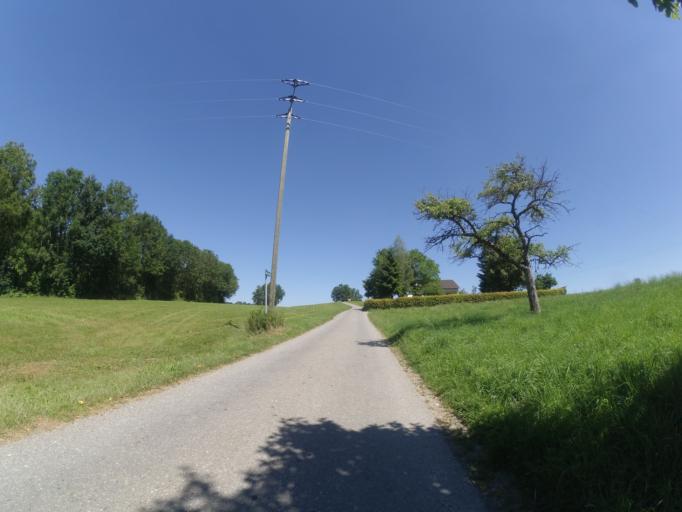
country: DE
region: Baden-Wuerttemberg
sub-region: Tuebingen Region
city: Bad Wurzach
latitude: 47.8933
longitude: 9.9056
